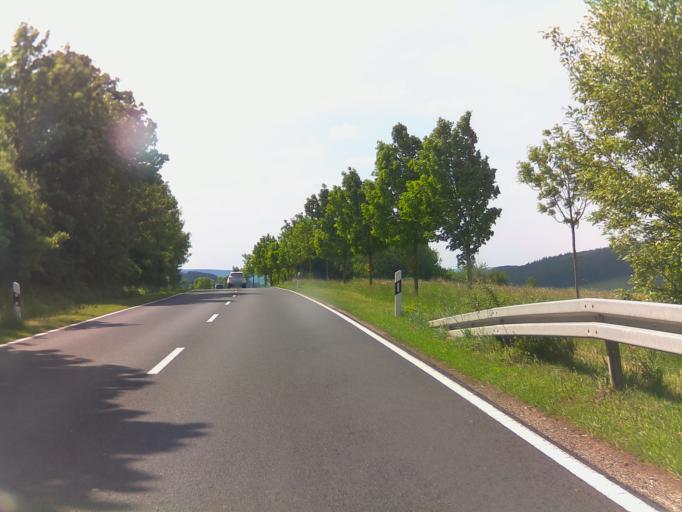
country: DE
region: Hesse
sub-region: Regierungsbezirk Kassel
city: Hofbieber
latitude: 50.6139
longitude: 9.9145
